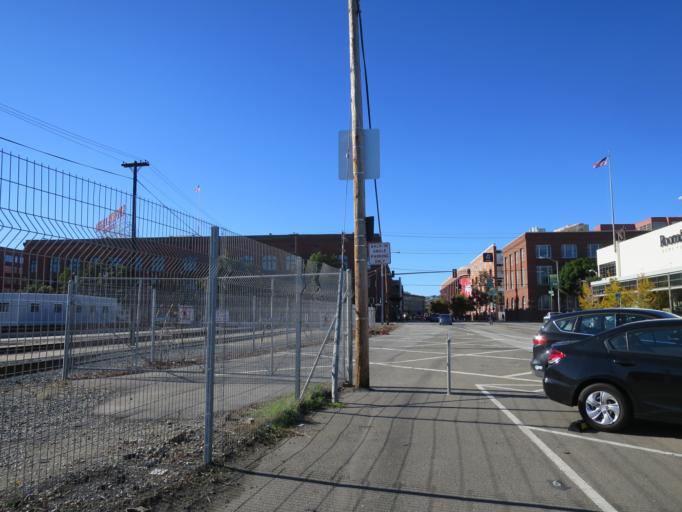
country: US
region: California
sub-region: San Francisco County
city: San Francisco
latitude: 37.7723
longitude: -122.4009
